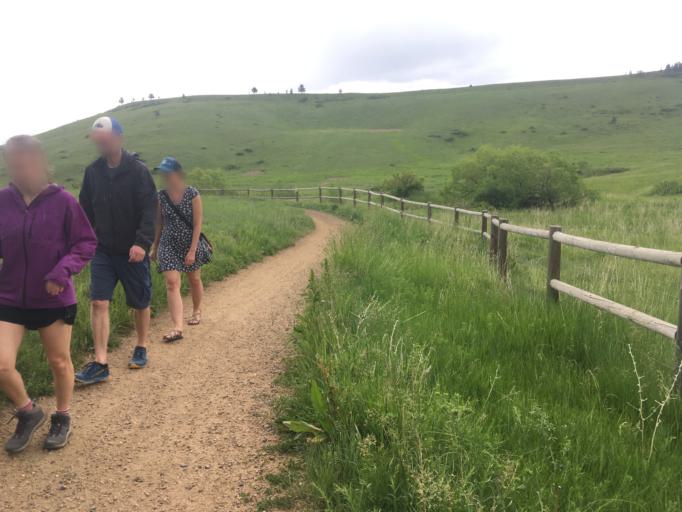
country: US
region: Colorado
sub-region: Boulder County
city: Boulder
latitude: 39.9308
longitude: -105.2581
